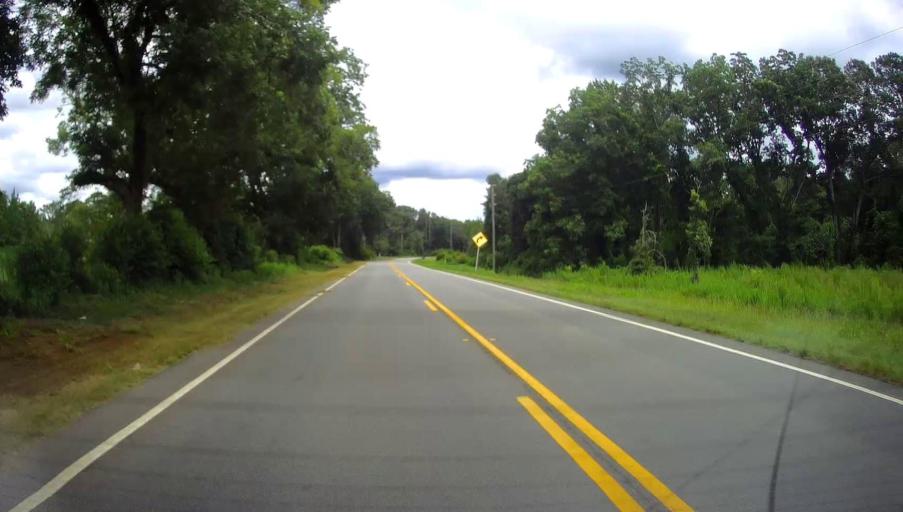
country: US
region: Georgia
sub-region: Macon County
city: Oglethorpe
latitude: 32.2836
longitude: -84.1653
